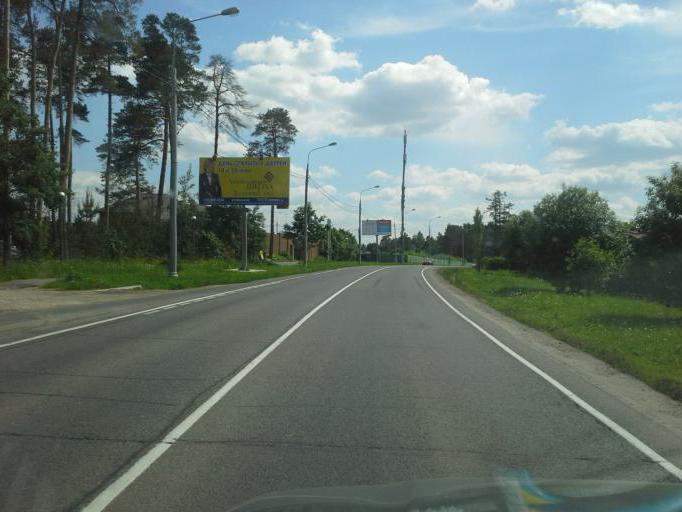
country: RU
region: Moskovskaya
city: Barvikha
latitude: 55.7112
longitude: 37.2708
